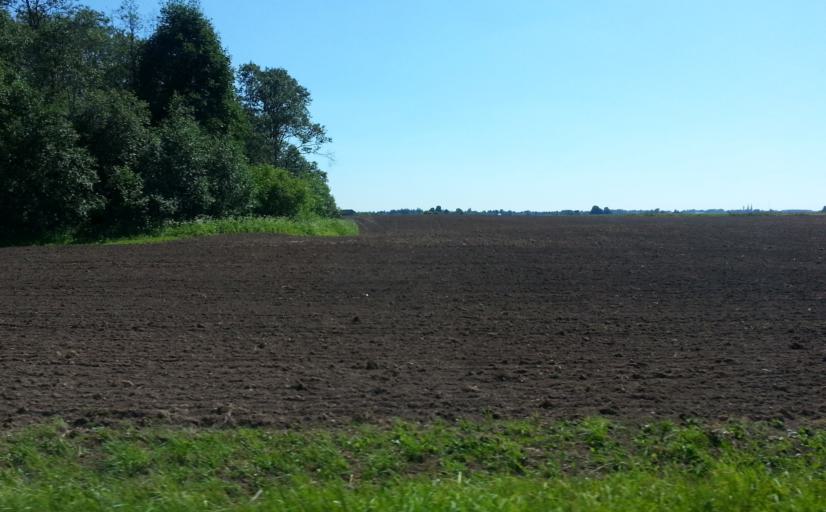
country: LT
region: Panevezys
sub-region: Birzai
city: Birzai
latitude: 56.2116
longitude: 24.6814
